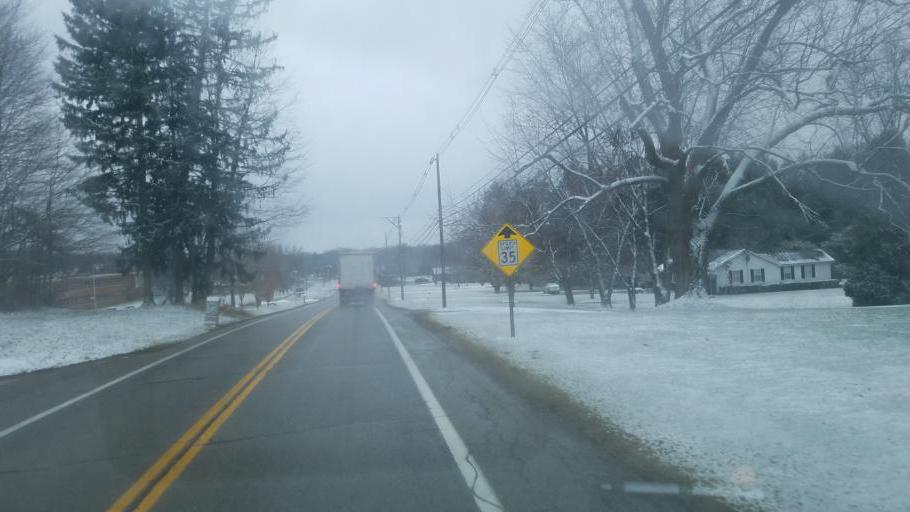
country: US
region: Ohio
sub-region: Portage County
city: Garrettsville
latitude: 41.2693
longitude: -81.1018
